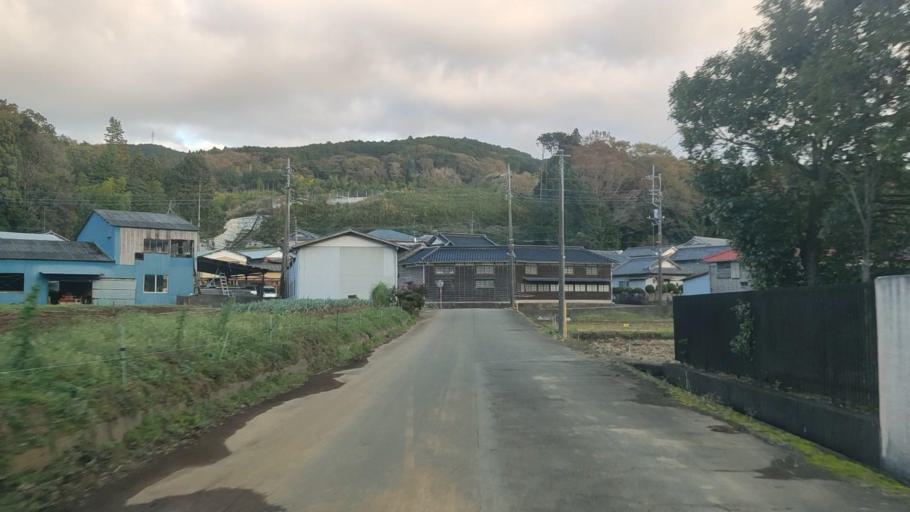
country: JP
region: Kanagawa
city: Yugawara
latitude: 35.1275
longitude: 139.0148
